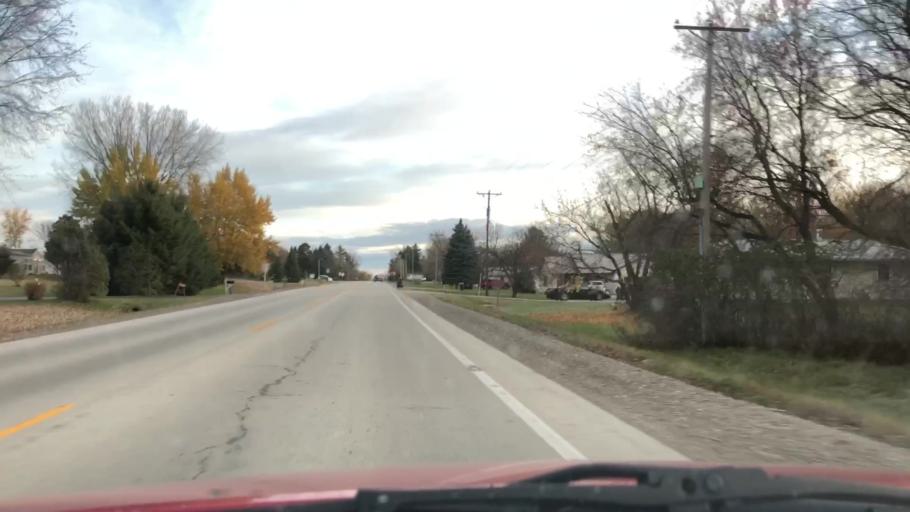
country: US
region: Wisconsin
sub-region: Brown County
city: Oneida
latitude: 44.4424
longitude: -88.2285
